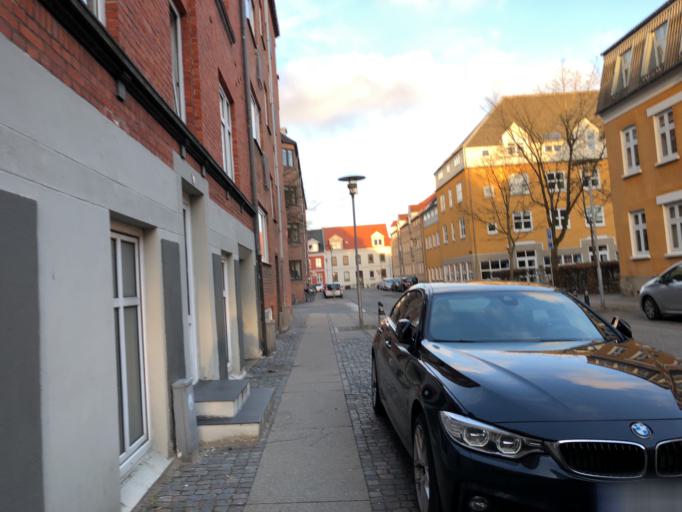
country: DK
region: North Denmark
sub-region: Alborg Kommune
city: Aalborg
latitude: 57.0514
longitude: 9.9060
